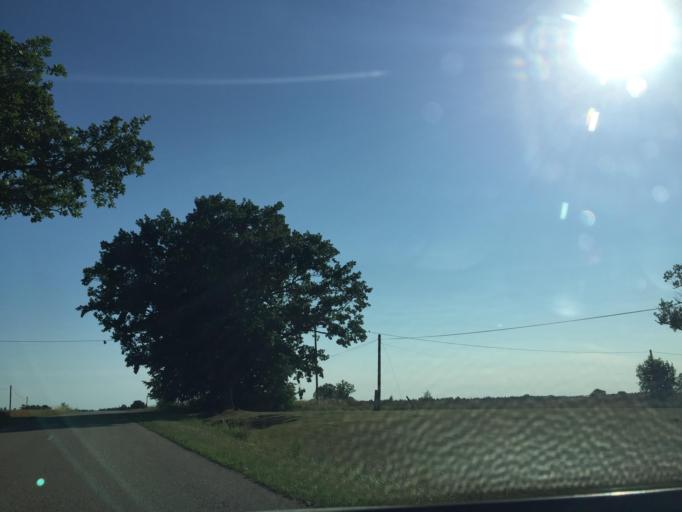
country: LV
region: Talsu Rajons
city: Stende
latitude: 57.1456
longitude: 22.6269
